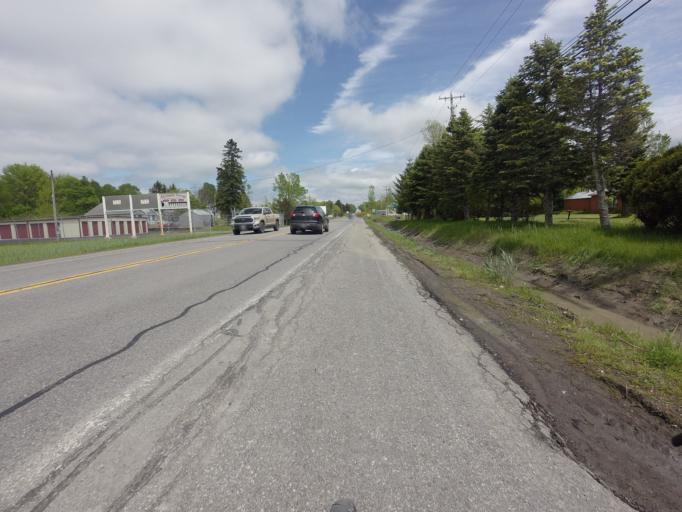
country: CA
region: Ontario
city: Cornwall
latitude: 44.9780
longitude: -74.7035
